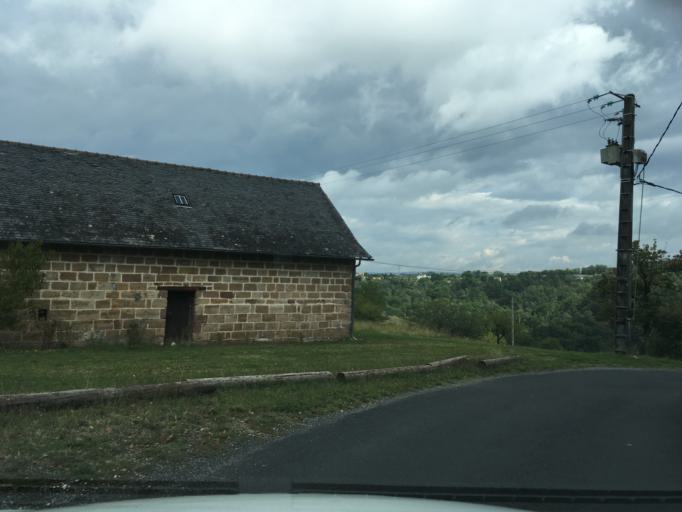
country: FR
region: Limousin
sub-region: Departement de la Correze
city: Brive-la-Gaillarde
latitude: 45.1136
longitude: 1.5477
